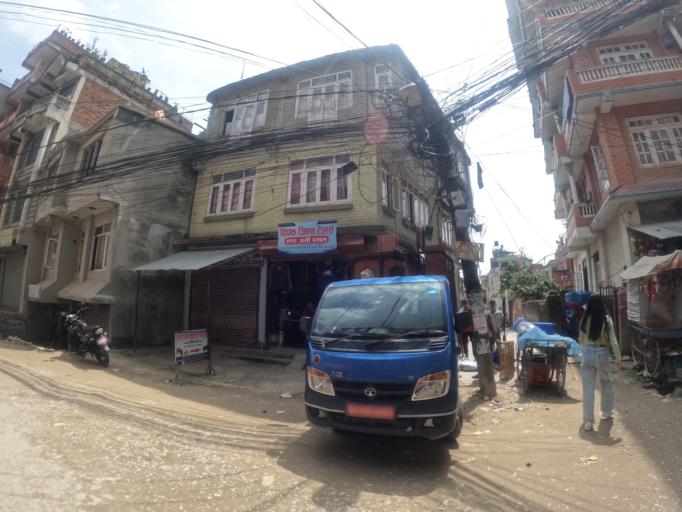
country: NP
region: Central Region
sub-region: Bagmati Zone
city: Bhaktapur
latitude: 27.6846
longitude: 85.3880
